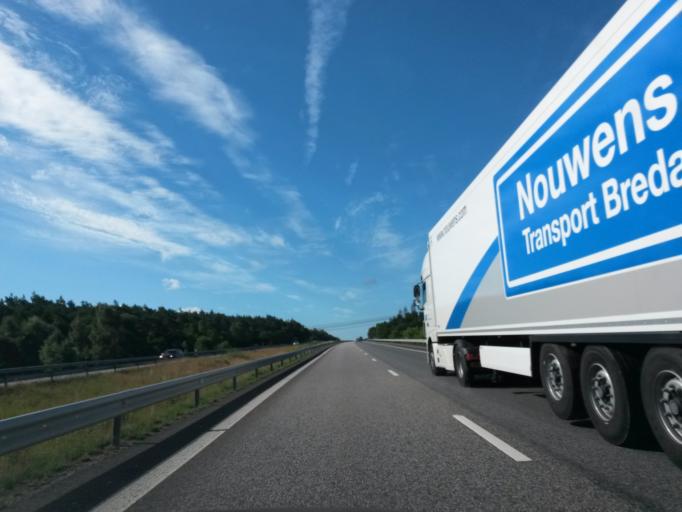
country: SE
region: Halland
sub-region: Kungsbacka Kommun
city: Frillesas
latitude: 57.2877
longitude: 12.2159
